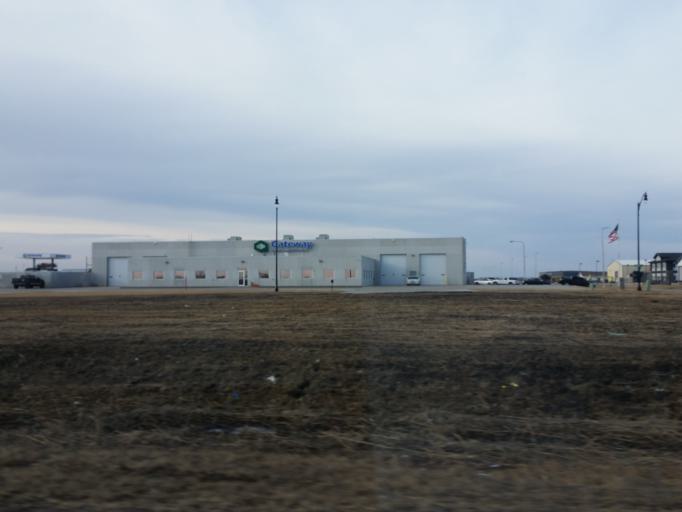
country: US
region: North Dakota
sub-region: Cass County
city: West Fargo
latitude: 46.8772
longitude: -96.9368
